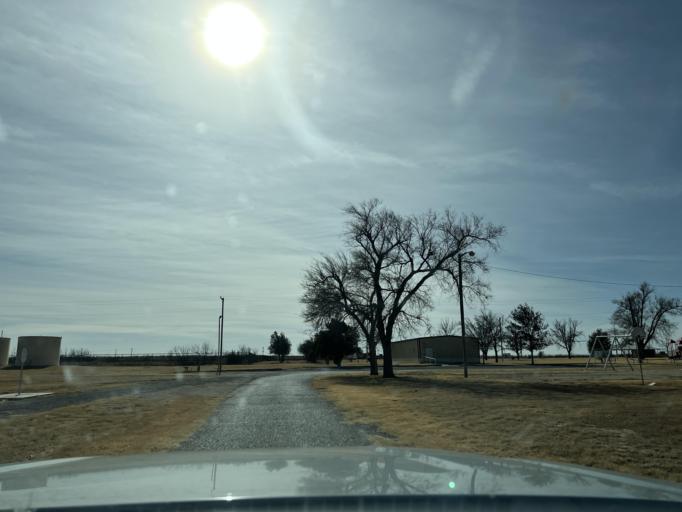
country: US
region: Texas
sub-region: Andrews County
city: Andrews
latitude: 32.4549
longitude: -102.5696
